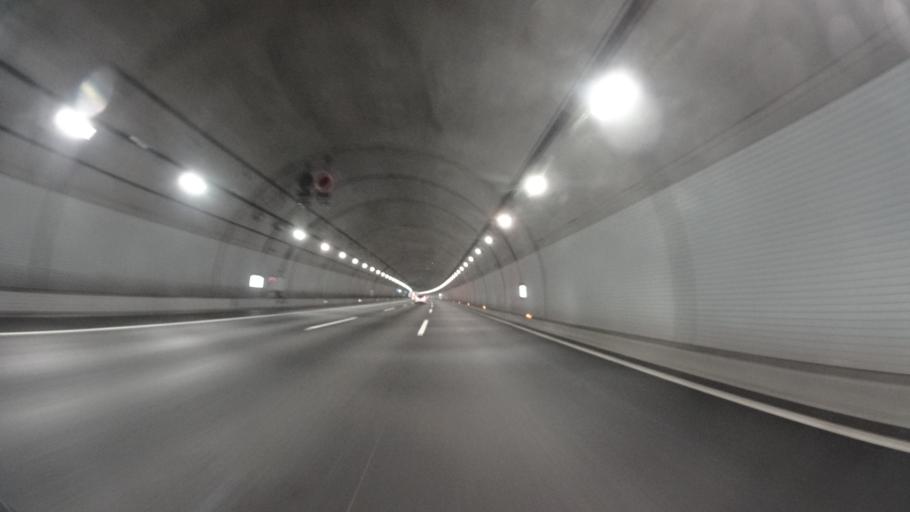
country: JP
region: Shizuoka
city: Shizuoka-shi
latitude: 35.0591
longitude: 138.4346
